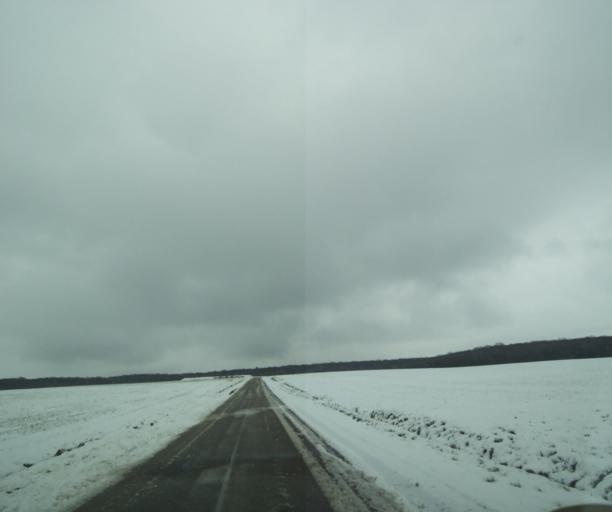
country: FR
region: Champagne-Ardenne
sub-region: Departement de la Haute-Marne
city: Laneuville-a-Remy
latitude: 48.3992
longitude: 4.8598
